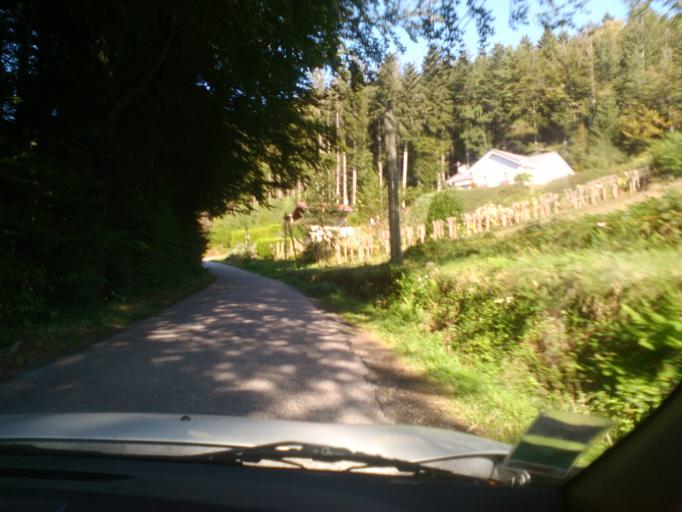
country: FR
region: Lorraine
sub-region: Departement des Vosges
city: Vagney
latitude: 48.0370
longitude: 6.7337
